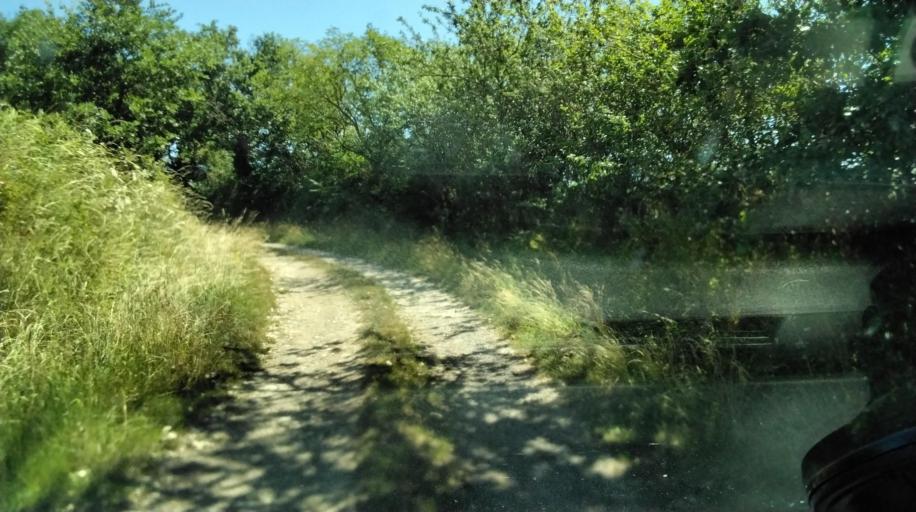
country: FR
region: Midi-Pyrenees
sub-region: Departement de la Haute-Garonne
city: Sainte-Foy-de-Peyrolieres
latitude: 43.4826
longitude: 1.1144
